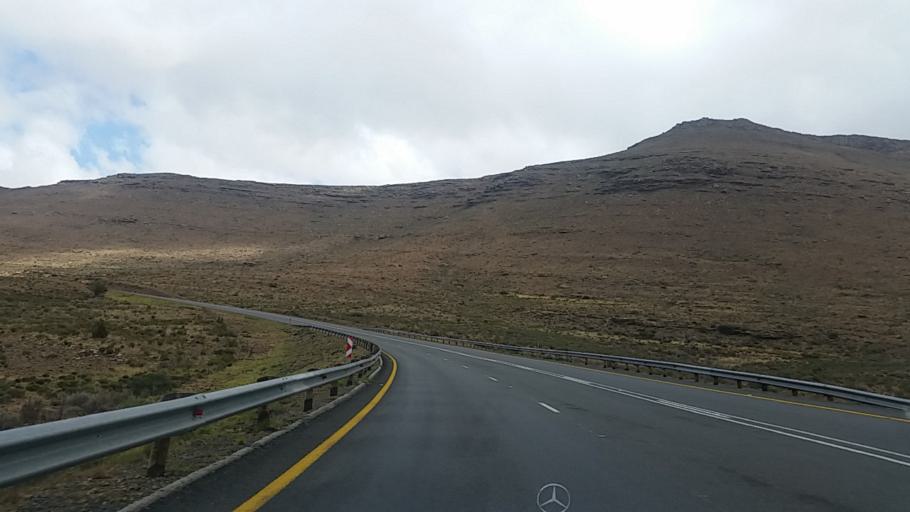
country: ZA
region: Eastern Cape
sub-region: Chris Hani District Municipality
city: Middelburg
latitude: -31.8181
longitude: 24.8606
